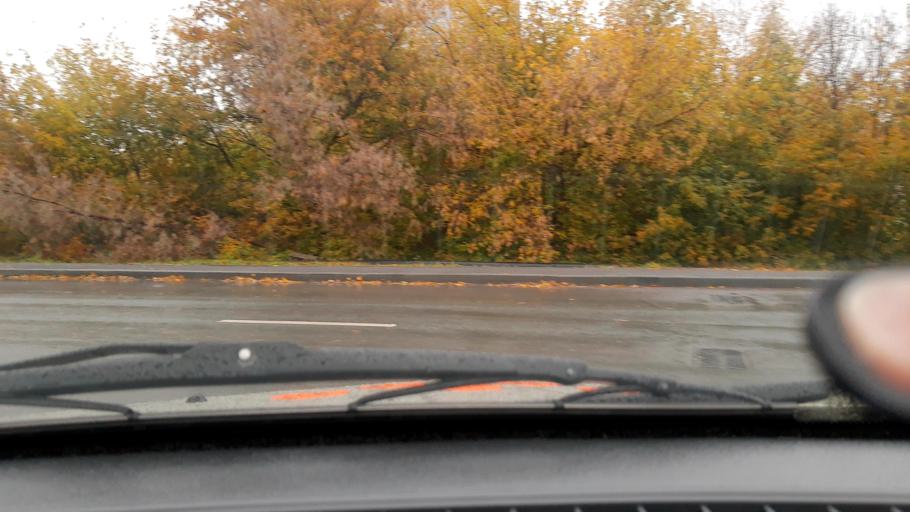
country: RU
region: Bashkortostan
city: Ufa
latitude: 54.7218
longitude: 56.0005
